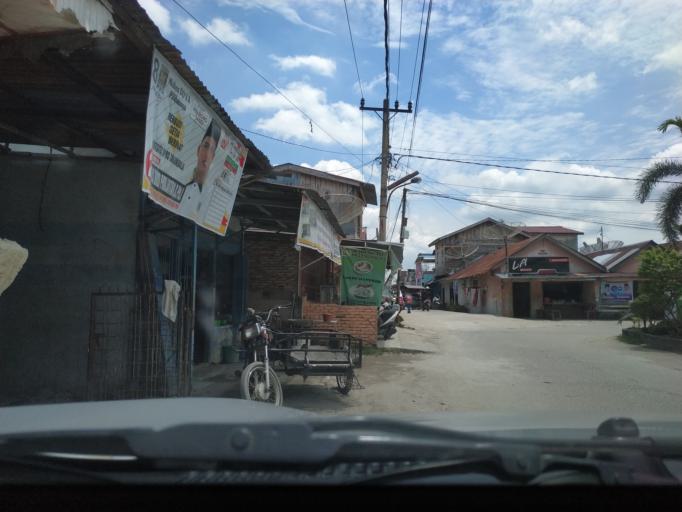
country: ID
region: North Sumatra
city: Tanjungbalai
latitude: 2.9623
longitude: 99.8111
